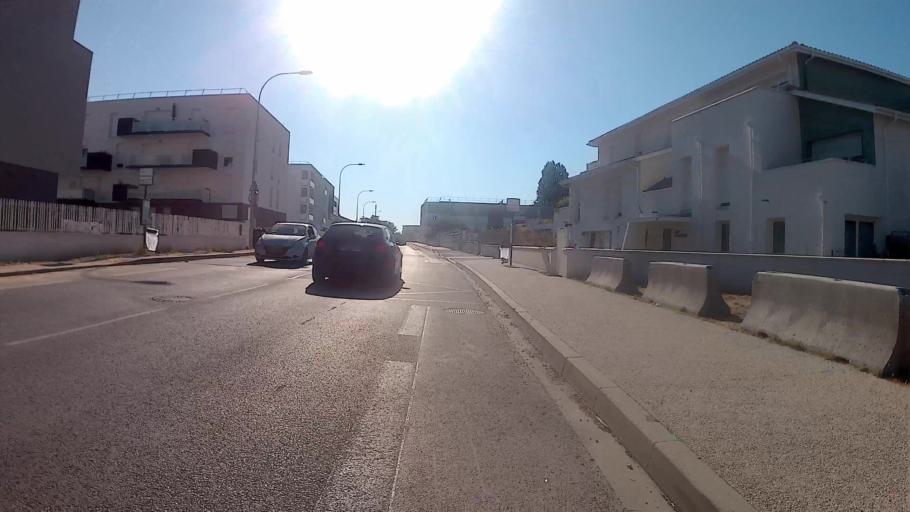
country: FR
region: Aquitaine
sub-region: Departement de la Gironde
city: Villenave-d'Ornon
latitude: 44.7812
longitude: -0.5593
